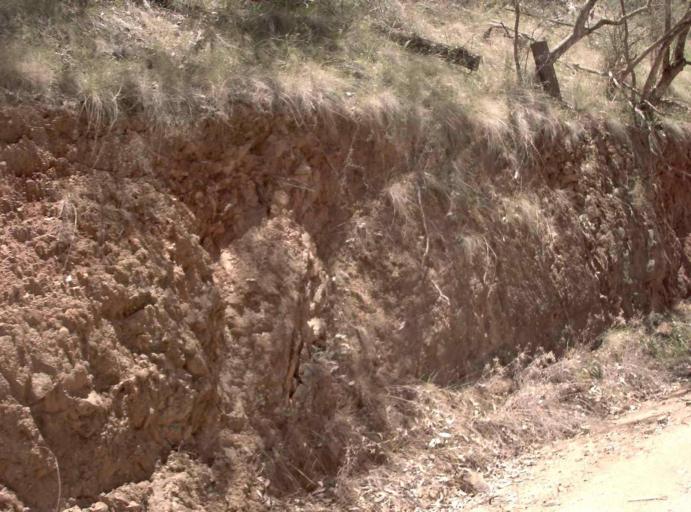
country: AU
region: New South Wales
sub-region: Snowy River
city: Jindabyne
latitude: -36.9283
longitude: 148.3716
